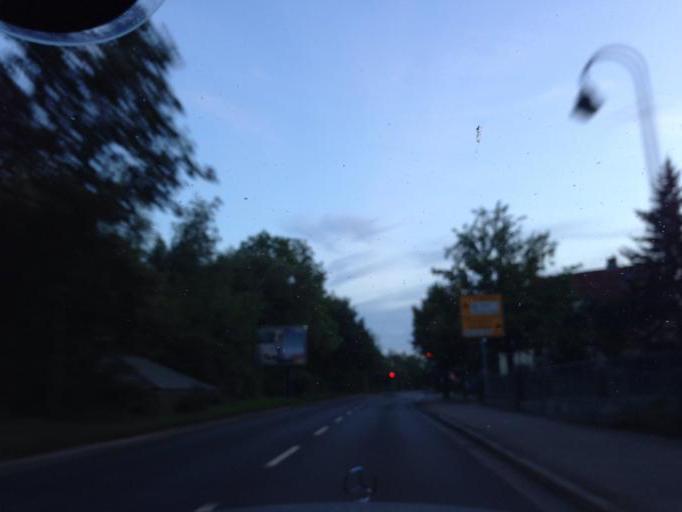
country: DE
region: Schleswig-Holstein
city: Ahrensburg
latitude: 53.6745
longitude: 10.2450
